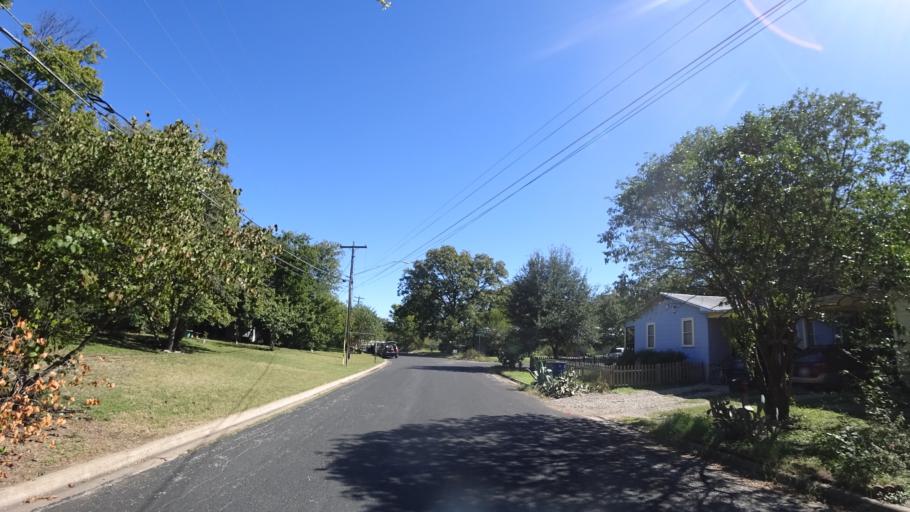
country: US
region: Texas
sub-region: Travis County
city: Austin
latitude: 30.2893
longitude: -97.7145
